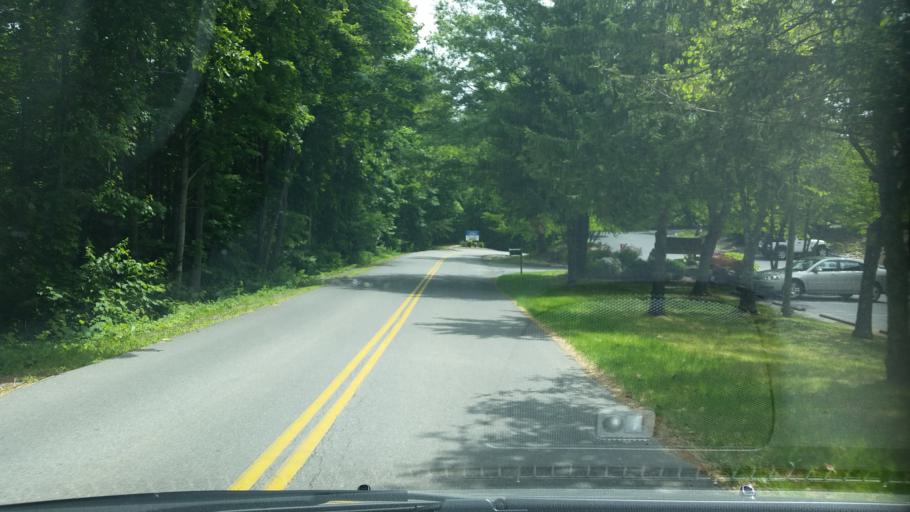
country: US
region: Tennessee
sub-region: Sevier County
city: Gatlinburg
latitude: 35.7132
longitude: -83.5311
